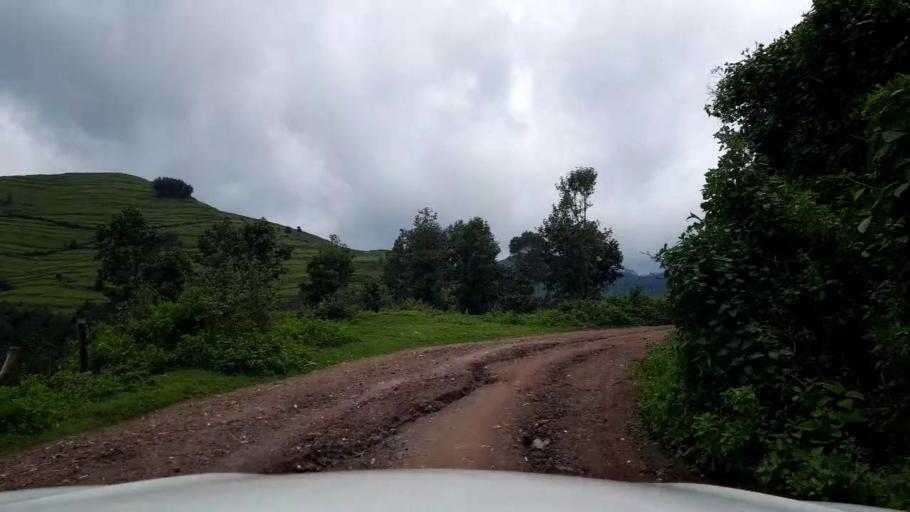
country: RW
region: Western Province
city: Gisenyi
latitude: -1.6503
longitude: 29.4152
